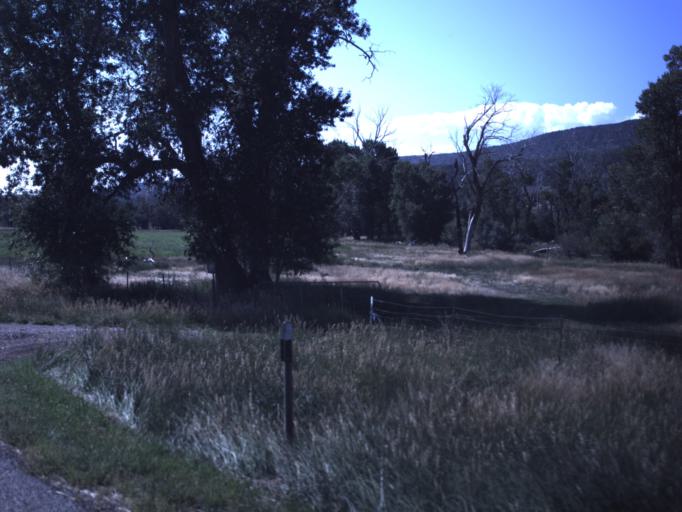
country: US
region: Utah
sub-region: Duchesne County
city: Duchesne
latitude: 40.3798
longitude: -110.7369
